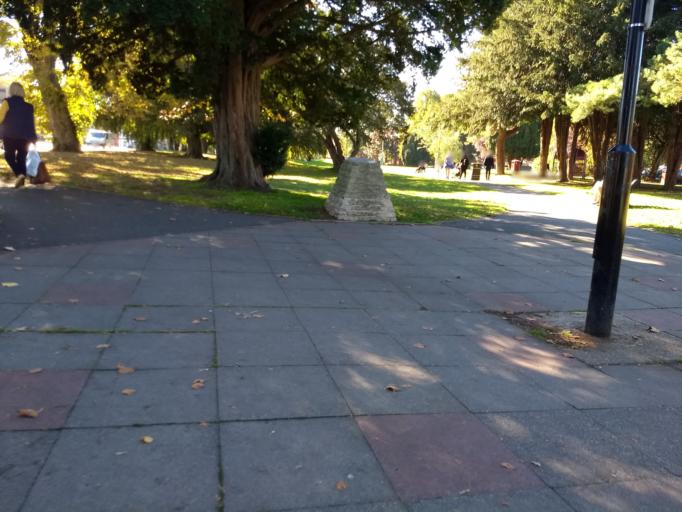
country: GB
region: England
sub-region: Isle of Wight
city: Newport
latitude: 50.6978
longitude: -1.2931
